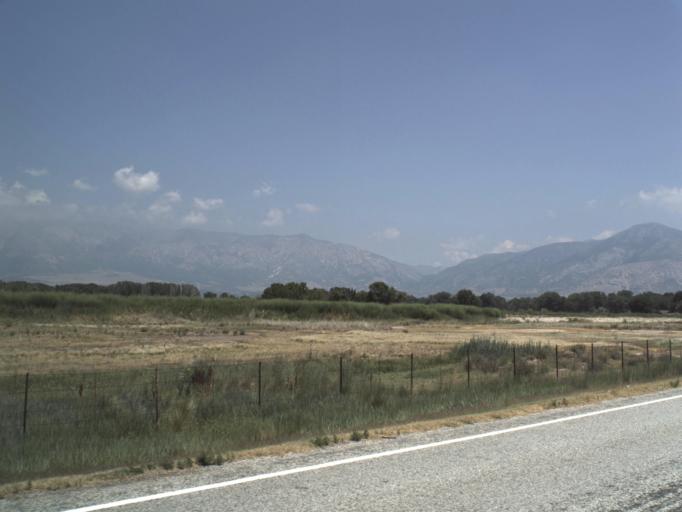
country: US
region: Utah
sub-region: Weber County
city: Marriott-Slaterville
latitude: 41.2443
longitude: -112.0577
